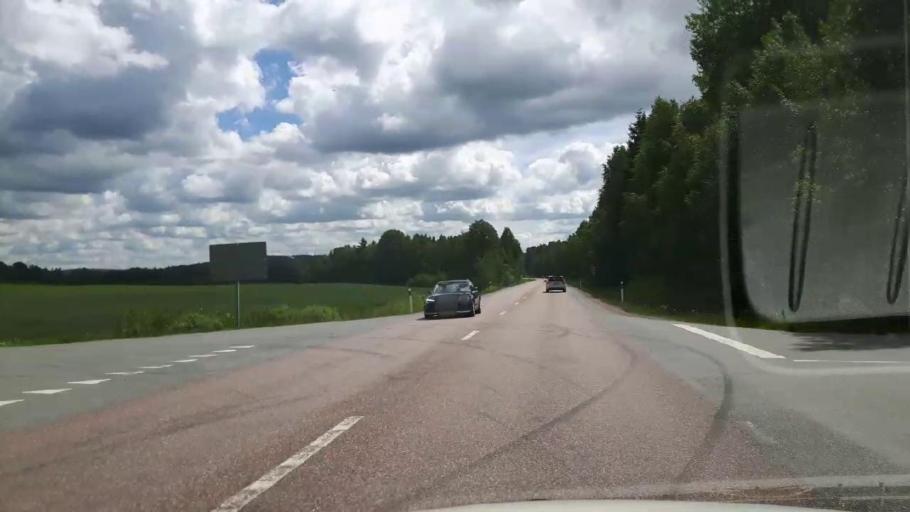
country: SE
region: Dalarna
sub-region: Saters Kommun
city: Saeter
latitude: 60.4790
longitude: 15.7787
